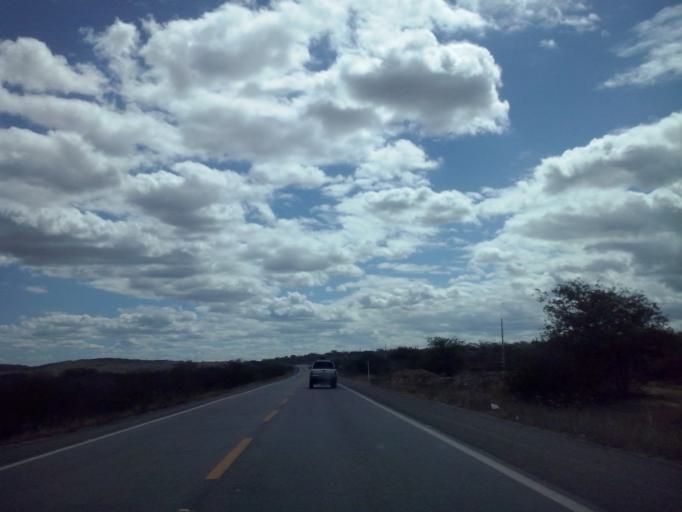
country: BR
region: Paraiba
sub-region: Soledade
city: Soledade
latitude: -7.0446
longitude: -36.3949
